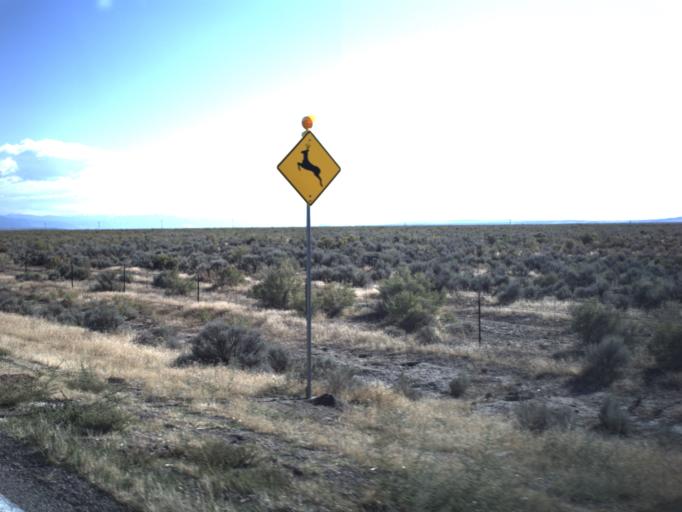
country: US
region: Utah
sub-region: Millard County
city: Delta
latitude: 39.2491
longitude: -112.4385
